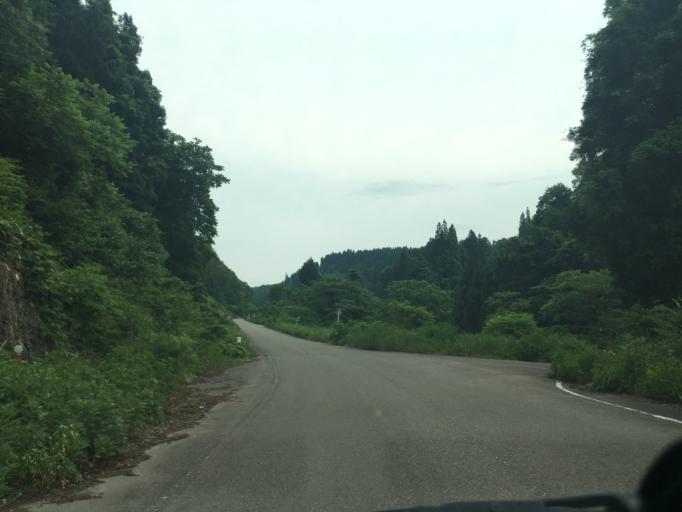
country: JP
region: Fukushima
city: Kitakata
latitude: 37.4762
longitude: 139.7738
